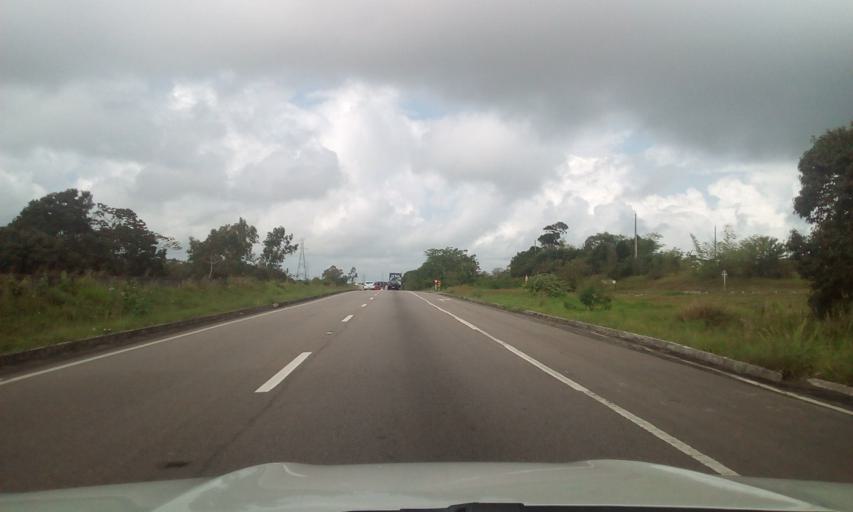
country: BR
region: Paraiba
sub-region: Conde
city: Conde
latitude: -7.3002
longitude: -34.9389
